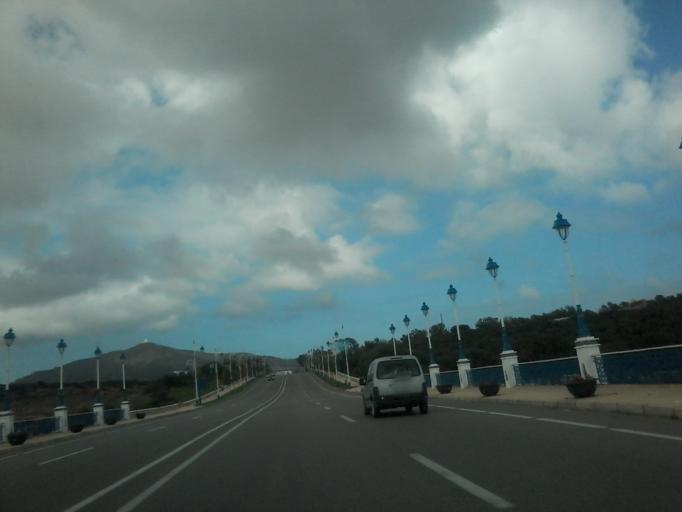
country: MA
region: Tanger-Tetouan
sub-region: Tetouan
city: Martil
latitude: 35.6445
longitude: -5.2932
